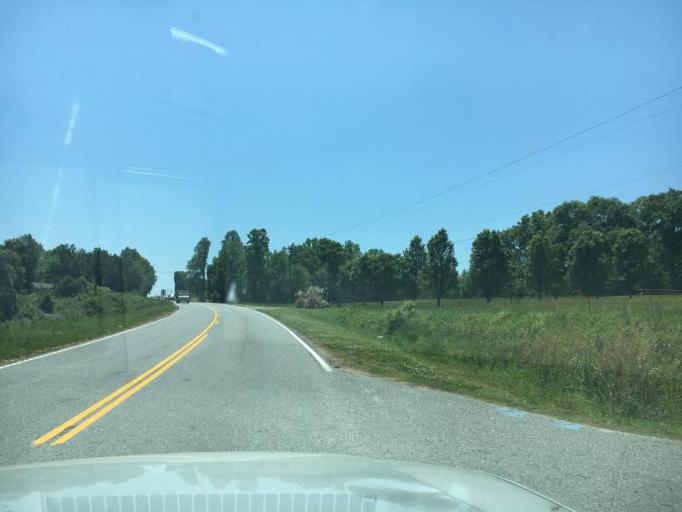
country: US
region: South Carolina
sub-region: Cherokee County
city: East Gaffney
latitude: 35.1168
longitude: -81.5997
